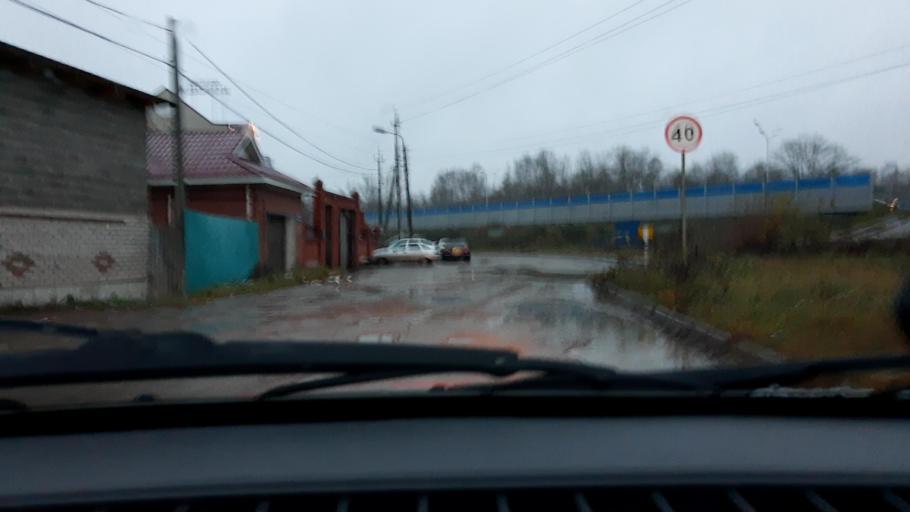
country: RU
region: Bashkortostan
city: Ufa
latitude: 54.6940
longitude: 55.9452
